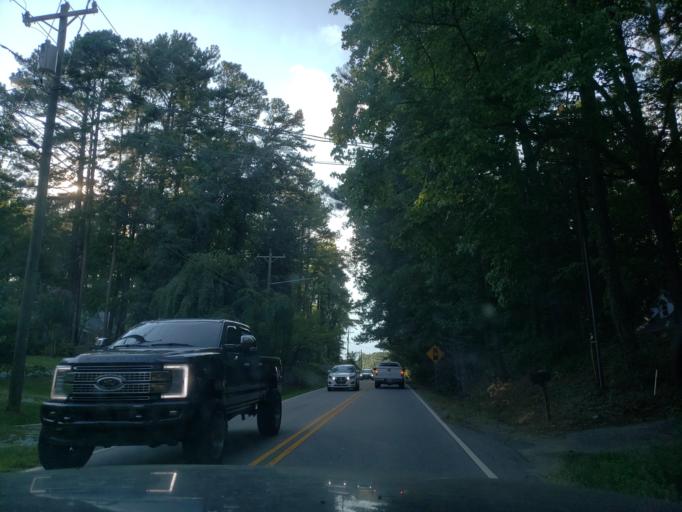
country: US
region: North Carolina
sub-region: Durham County
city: Durham
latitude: 35.9717
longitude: -78.9301
